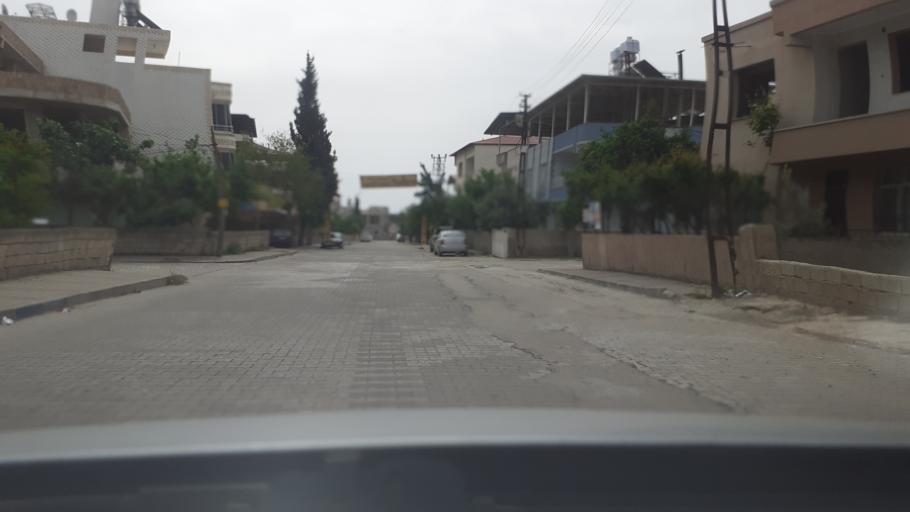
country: TR
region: Hatay
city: Kirikhan
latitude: 36.4947
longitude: 36.3649
